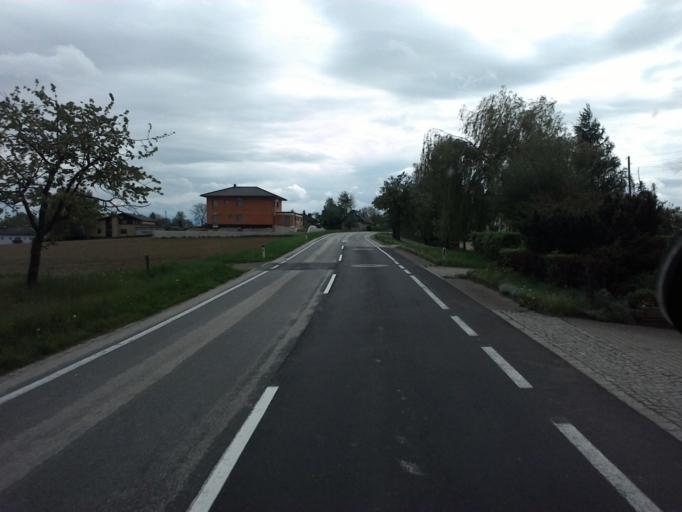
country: AT
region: Upper Austria
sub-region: Wels-Land
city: Sattledt
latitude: 48.0176
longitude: 14.0604
